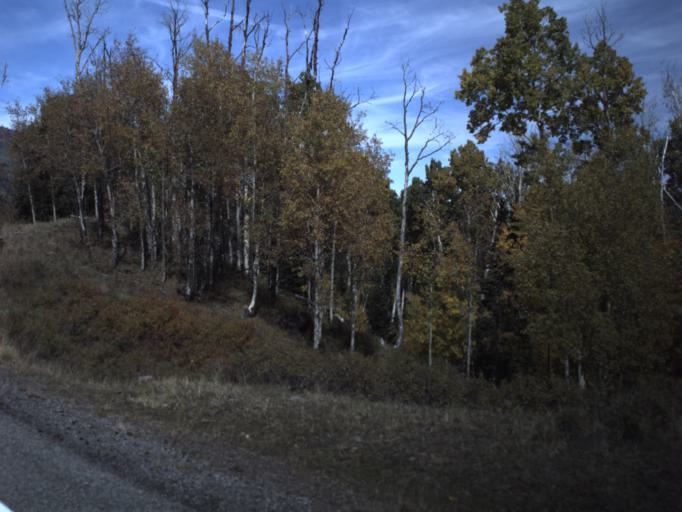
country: US
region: Utah
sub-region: Wayne County
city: Loa
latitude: 38.0716
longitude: -111.3374
